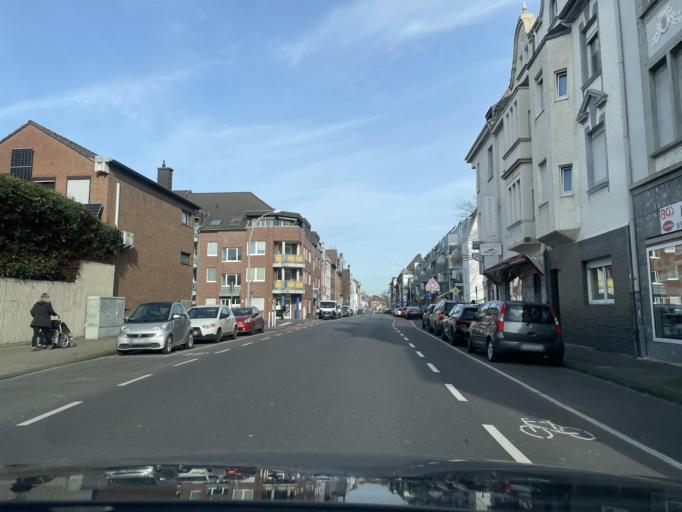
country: DE
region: North Rhine-Westphalia
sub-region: Regierungsbezirk Dusseldorf
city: Monchengladbach
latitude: 51.2093
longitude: 6.4472
